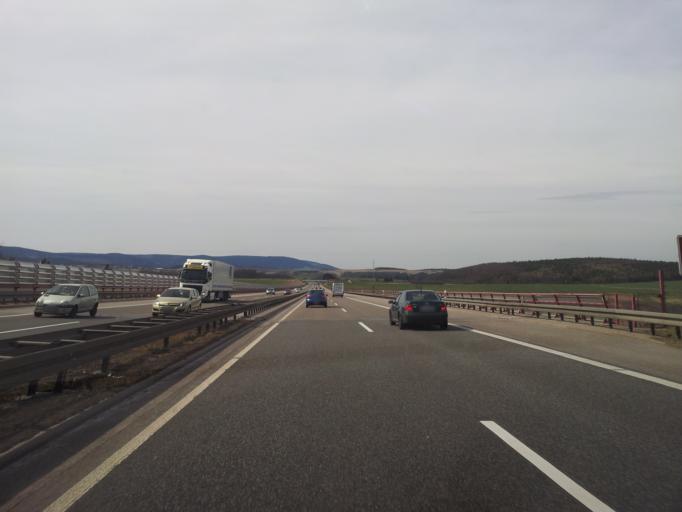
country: DE
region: Thuringia
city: Martinroda
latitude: 50.7149
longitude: 10.8773
